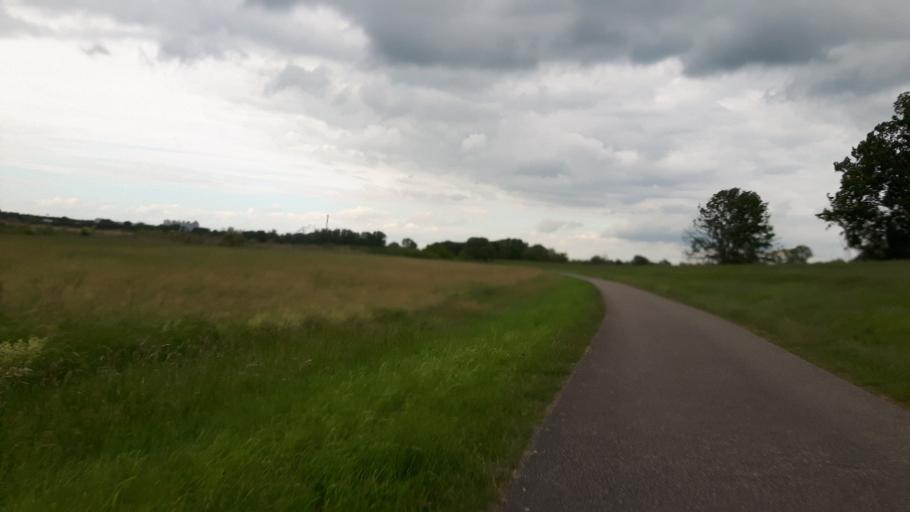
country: DE
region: Brandenburg
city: Schwedt (Oder)
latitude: 53.0630
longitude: 14.3163
